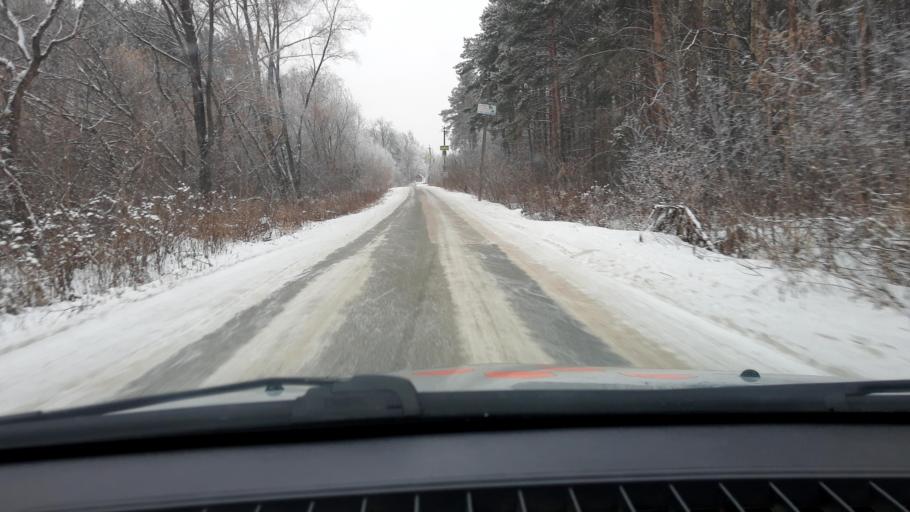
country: RU
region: Bashkortostan
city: Iglino
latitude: 54.8145
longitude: 56.1938
